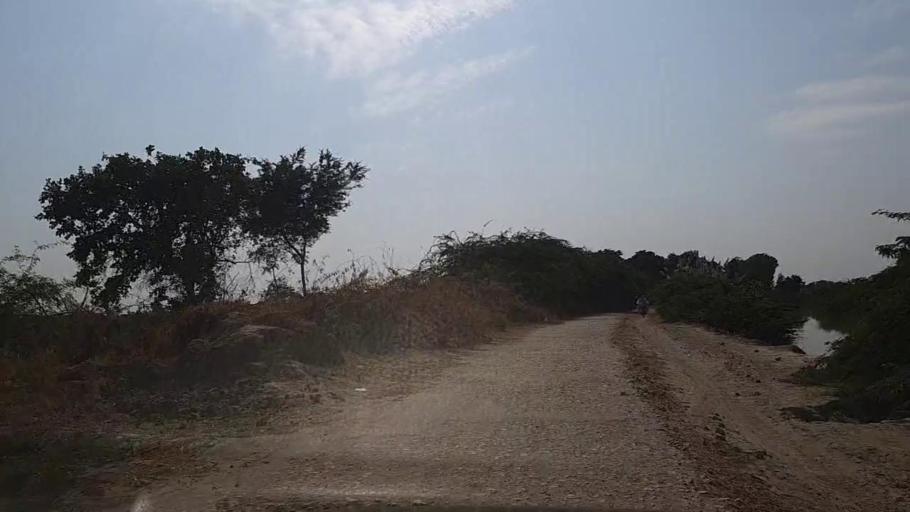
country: PK
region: Sindh
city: Thatta
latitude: 24.7496
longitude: 67.7742
